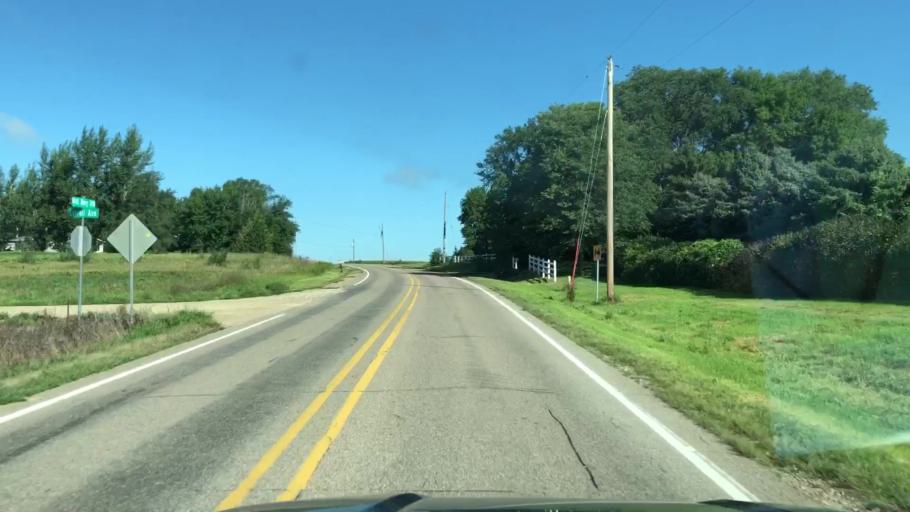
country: US
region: Iowa
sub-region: Woodbury County
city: Sergeant Bluff
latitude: 42.4247
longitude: -96.2770
